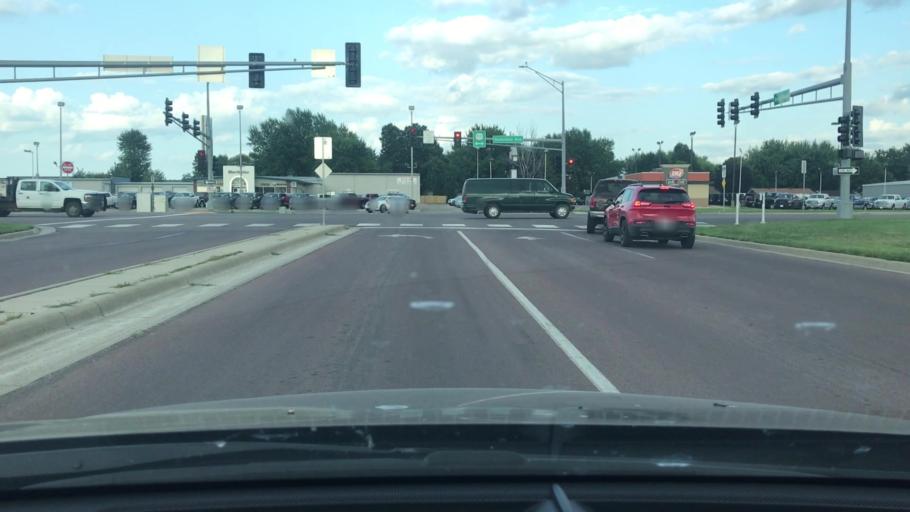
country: US
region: Minnesota
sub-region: Nobles County
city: Worthington
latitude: 43.6354
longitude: -95.5934
